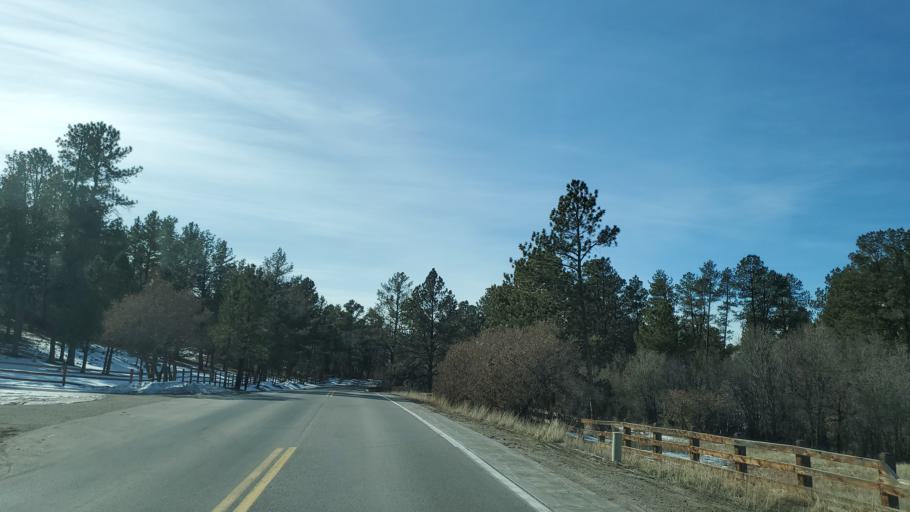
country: US
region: Colorado
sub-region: Douglas County
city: Castle Pines
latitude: 39.4438
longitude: -104.8828
